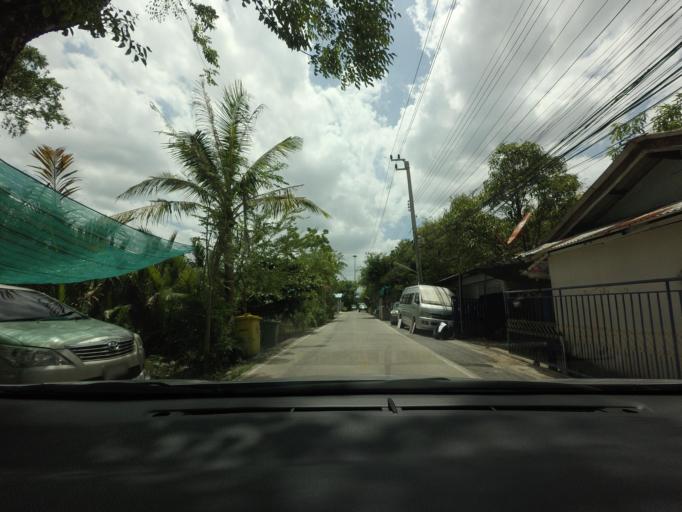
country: TH
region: Samut Prakan
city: Phra Samut Chedi
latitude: 13.6209
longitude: 100.5693
